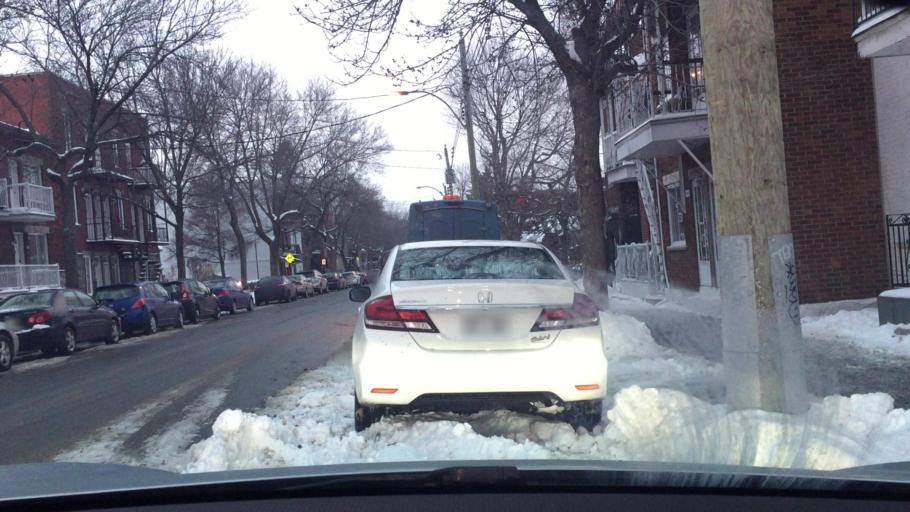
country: CA
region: Quebec
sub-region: Monteregie
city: Longueuil
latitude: 45.5350
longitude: -73.5521
